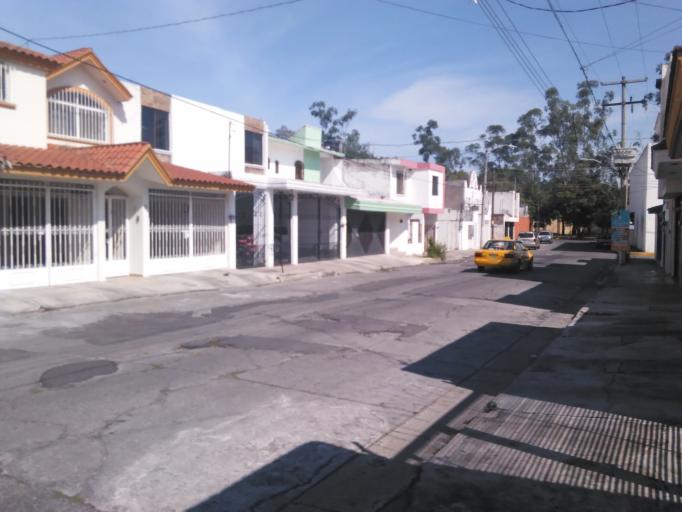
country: MX
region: Nayarit
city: Tepic
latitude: 21.4885
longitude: -104.8816
